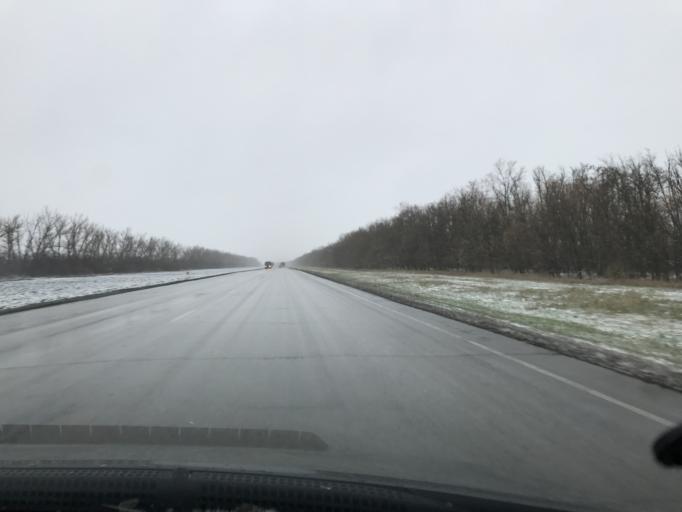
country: RU
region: Rostov
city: Yegorlykskaya
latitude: 46.6367
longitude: 40.5827
